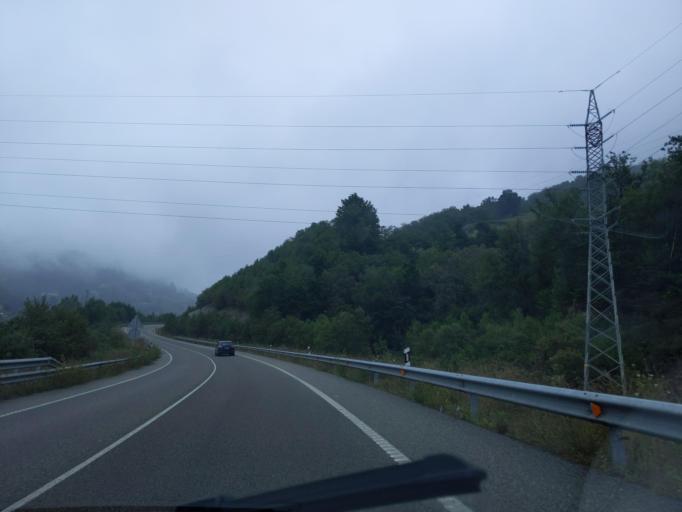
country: ES
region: Asturias
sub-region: Province of Asturias
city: El entrego
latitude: 43.2894
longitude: -5.6216
